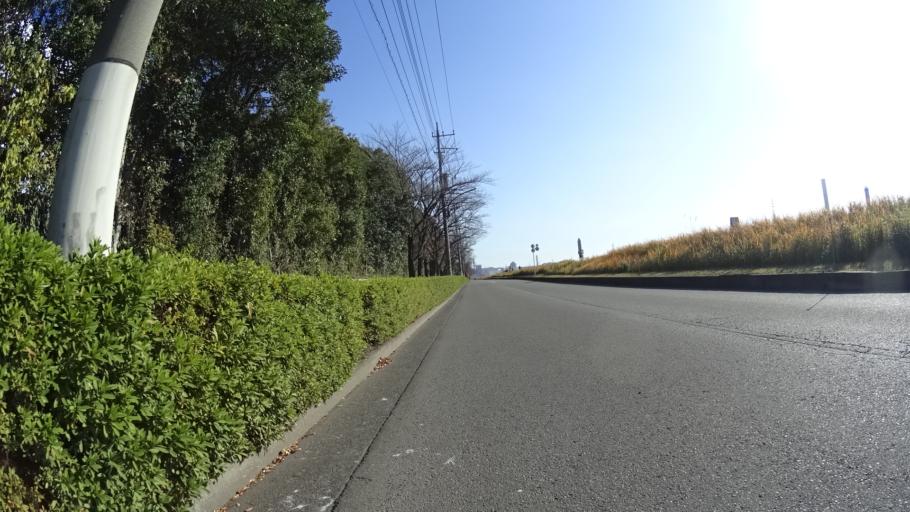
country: JP
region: Tokyo
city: Hino
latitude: 35.6715
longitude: 139.4307
